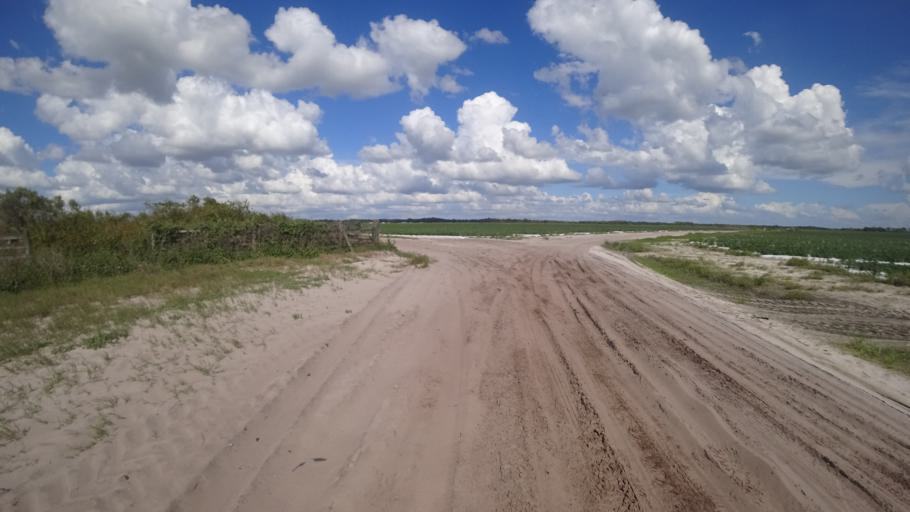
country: US
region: Florida
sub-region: DeSoto County
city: Arcadia
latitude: 27.3439
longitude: -82.0966
